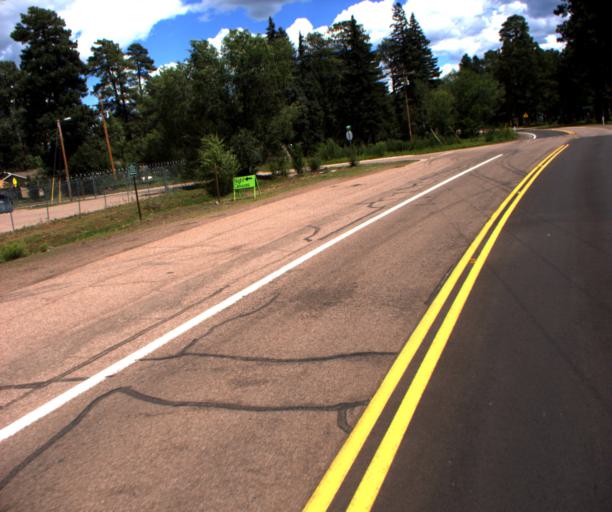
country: US
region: Arizona
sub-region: Navajo County
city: Pinetop-Lakeside
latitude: 34.0737
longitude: -109.8579
